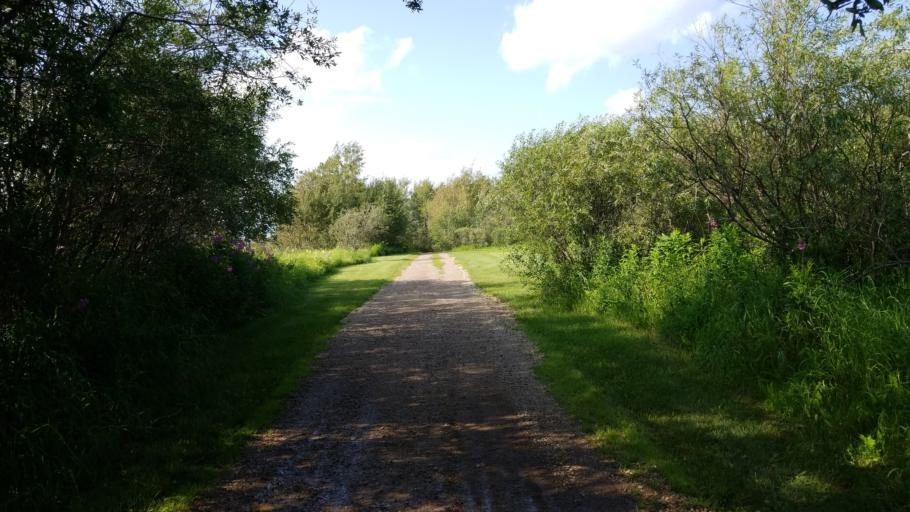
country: CA
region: Saskatchewan
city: Lloydminster
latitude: 53.2578
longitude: -110.0478
